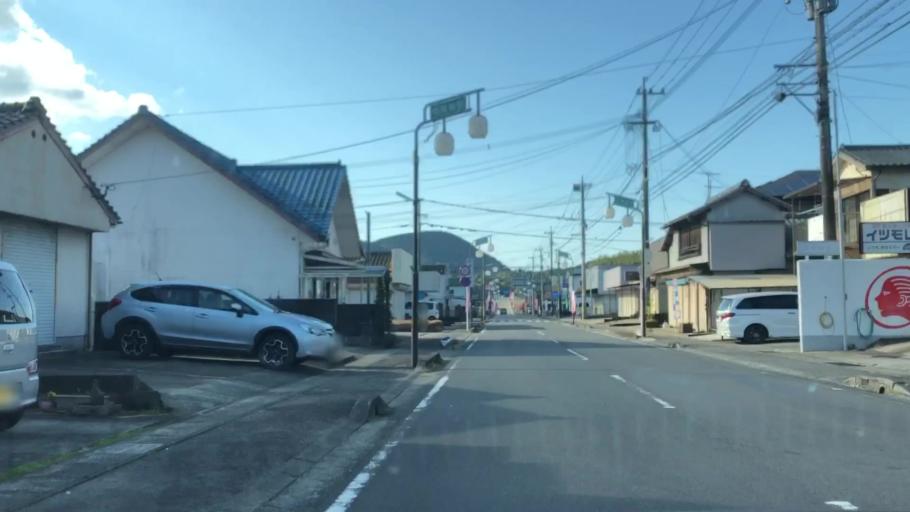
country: JP
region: Kagoshima
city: Satsumasendai
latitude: 31.8635
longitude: 130.3355
